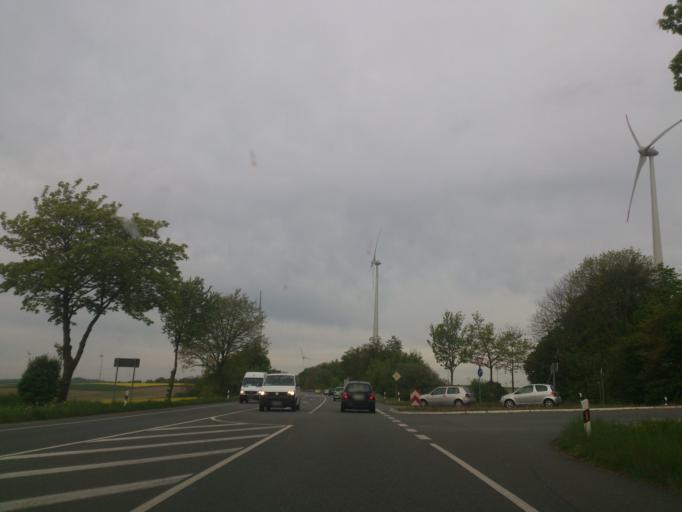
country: DE
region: North Rhine-Westphalia
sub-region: Regierungsbezirk Detmold
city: Altenbeken
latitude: 51.7382
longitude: 8.9345
